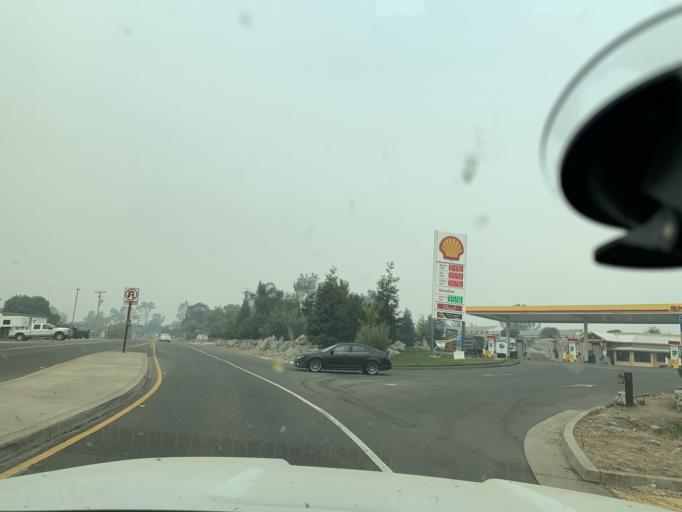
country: US
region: California
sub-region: Fresno County
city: Auberry
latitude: 37.0376
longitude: -119.5144
